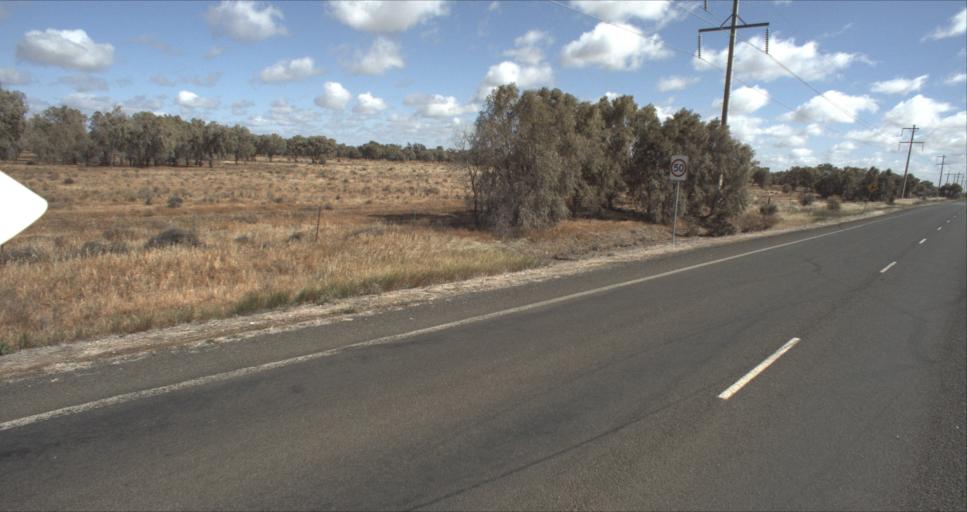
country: AU
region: New South Wales
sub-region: Murrumbidgee Shire
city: Darlington Point
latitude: -34.5186
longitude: 146.1762
